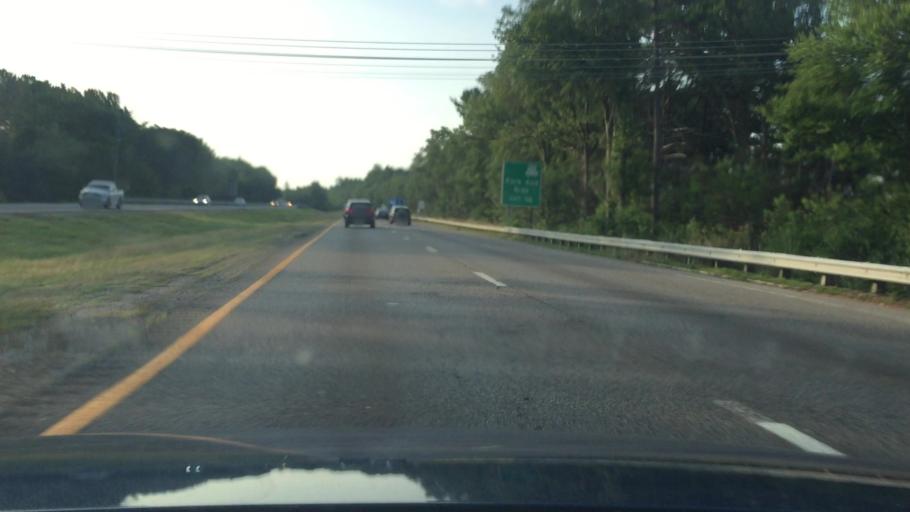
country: US
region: Massachusetts
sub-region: Plymouth County
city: Rockland
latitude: 42.1758
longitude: -70.9125
